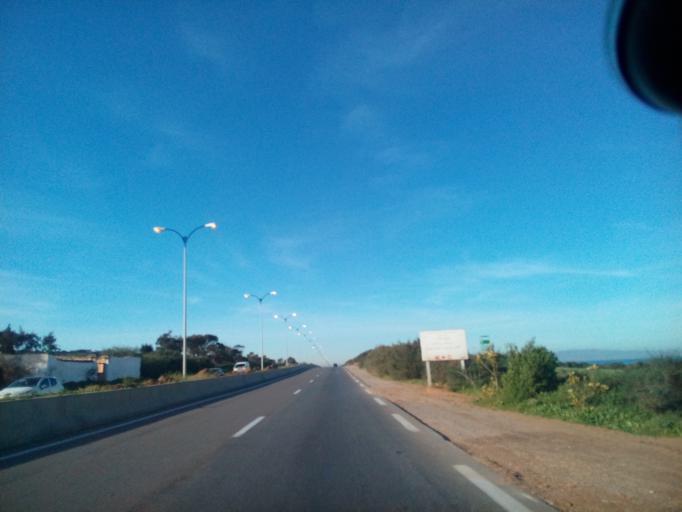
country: DZ
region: Mostaganem
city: Mostaganem
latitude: 35.8029
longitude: -0.0638
